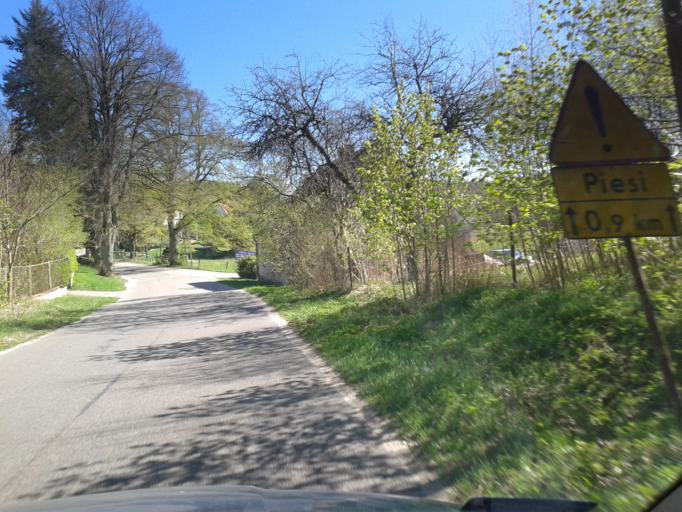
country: PL
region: West Pomeranian Voivodeship
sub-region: Powiat szczecinecki
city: Lubowo
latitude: 53.6326
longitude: 16.3427
